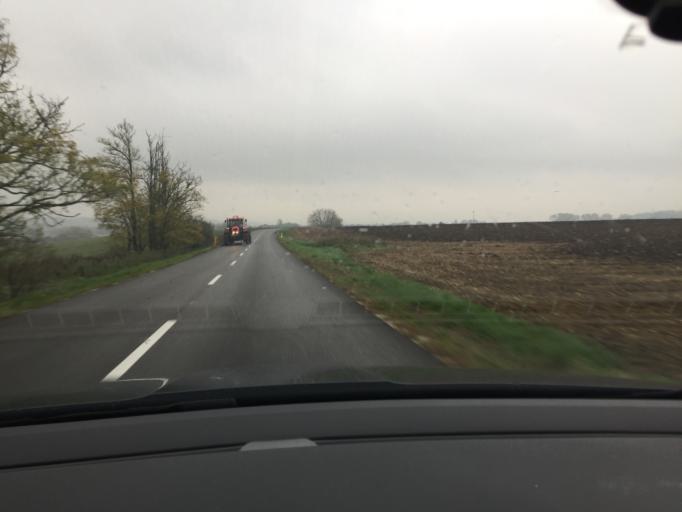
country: SK
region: Nitriansky
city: Zeliezovce
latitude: 48.0380
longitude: 18.8020
